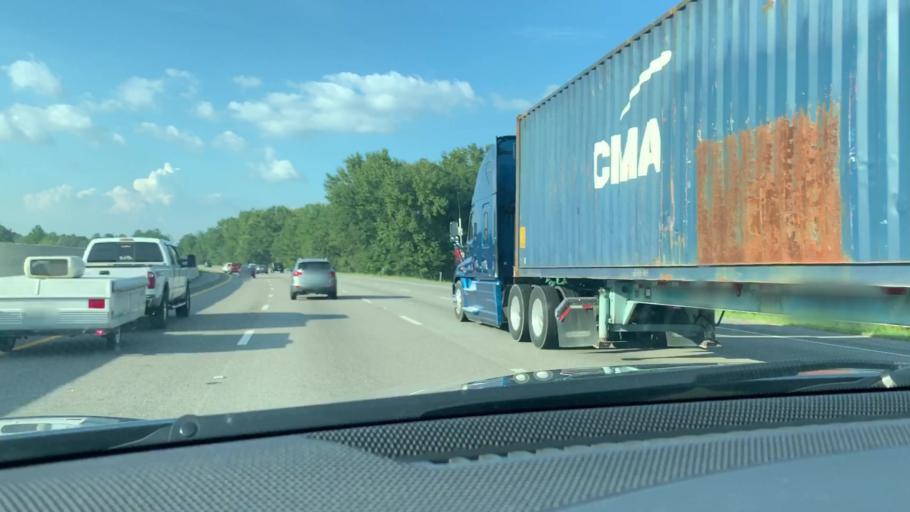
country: US
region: South Carolina
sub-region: Lexington County
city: Pineridge
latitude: 33.8832
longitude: -81.0370
